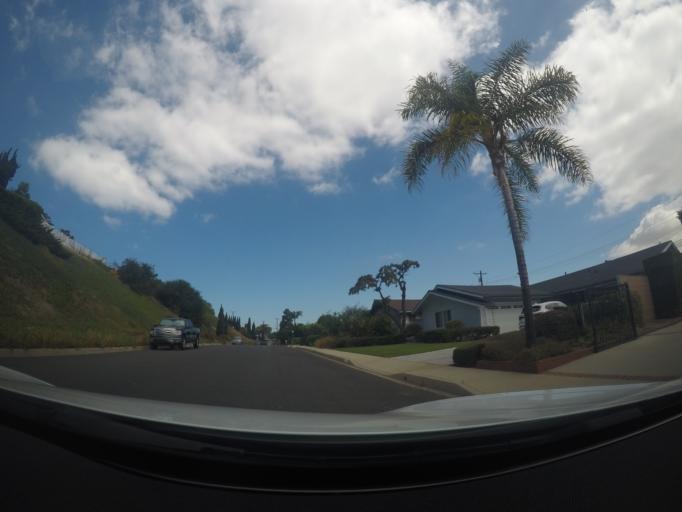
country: US
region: California
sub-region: Los Angeles County
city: Rolling Hills Estates
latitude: 33.8046
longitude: -118.3582
